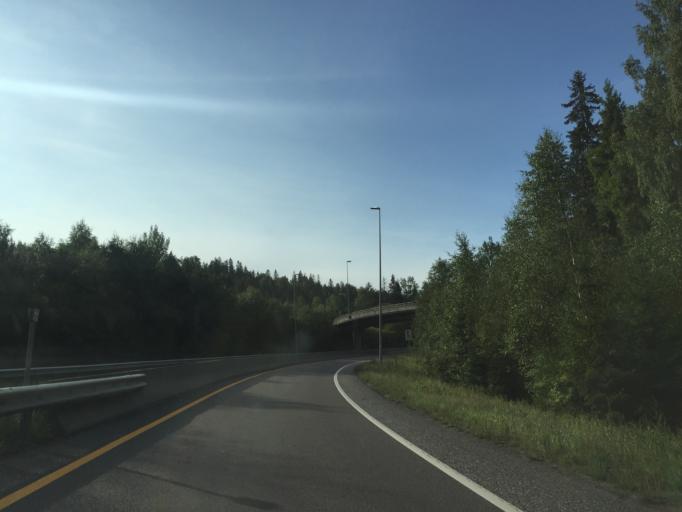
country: NO
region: Akershus
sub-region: Ski
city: Ski
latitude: 59.7412
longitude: 10.7821
